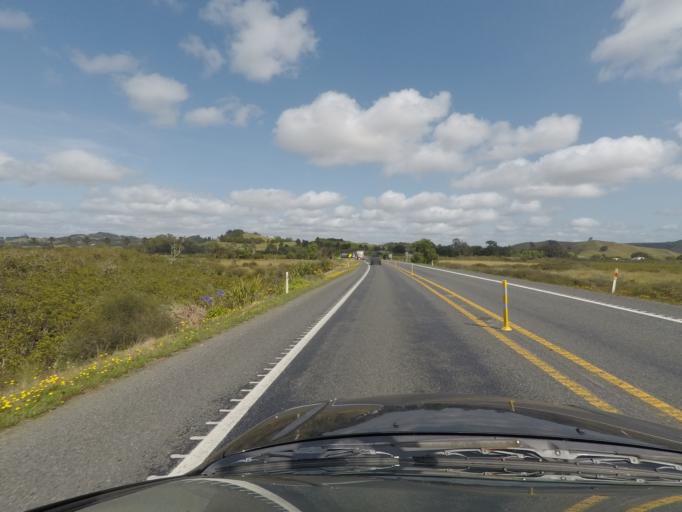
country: NZ
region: Northland
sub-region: Whangarei
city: Whangarei
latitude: -35.8353
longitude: 174.3197
